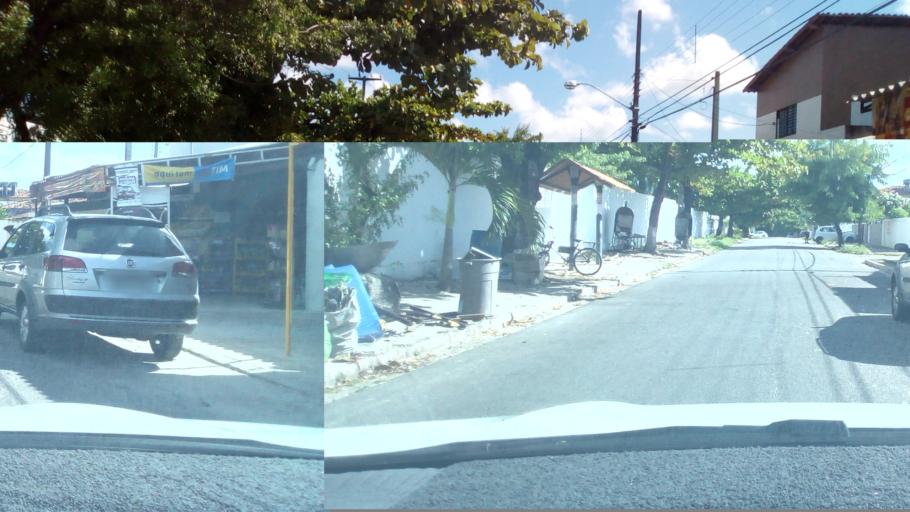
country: BR
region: Paraiba
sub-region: Joao Pessoa
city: Joao Pessoa
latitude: -7.1350
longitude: -34.8519
